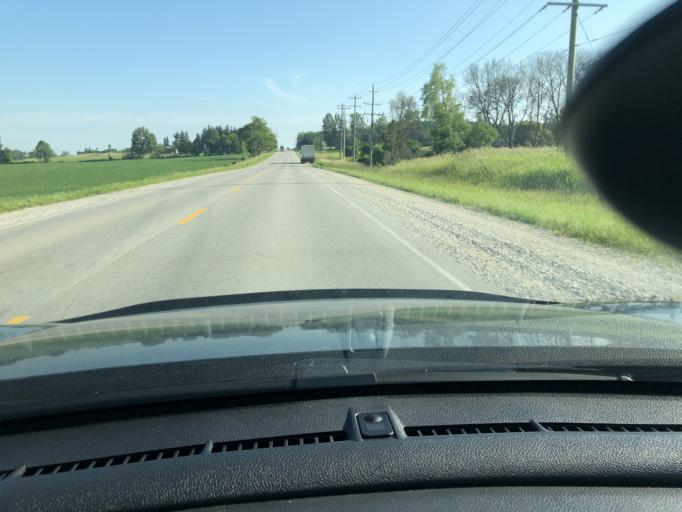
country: CA
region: Ontario
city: Stratford
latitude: 43.3939
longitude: -80.8374
